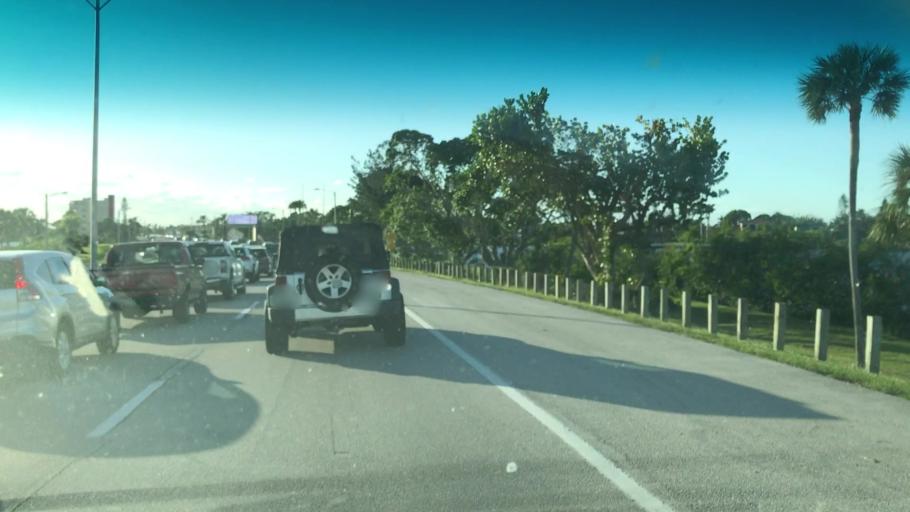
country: US
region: Florida
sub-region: Lee County
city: Cape Coral
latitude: 26.5625
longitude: -81.9330
